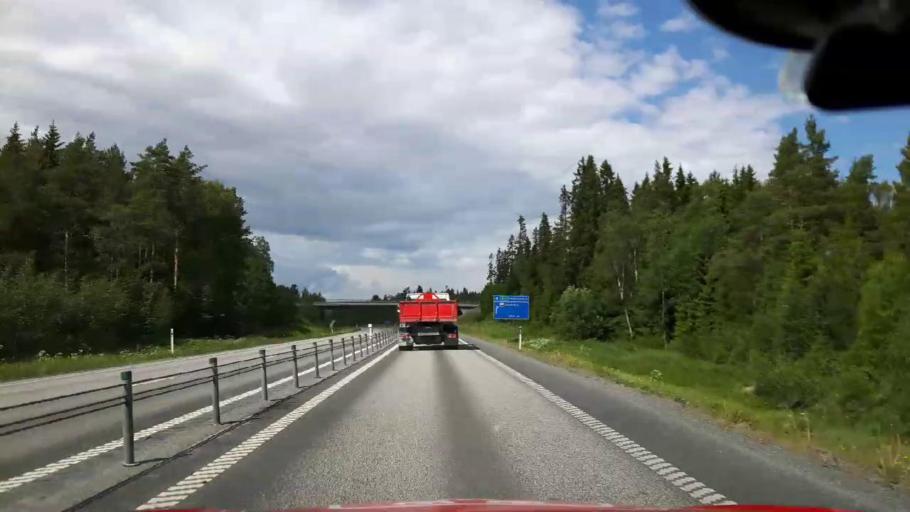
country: SE
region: Jaemtland
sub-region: OEstersunds Kommun
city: Ostersund
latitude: 63.2106
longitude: 14.6630
